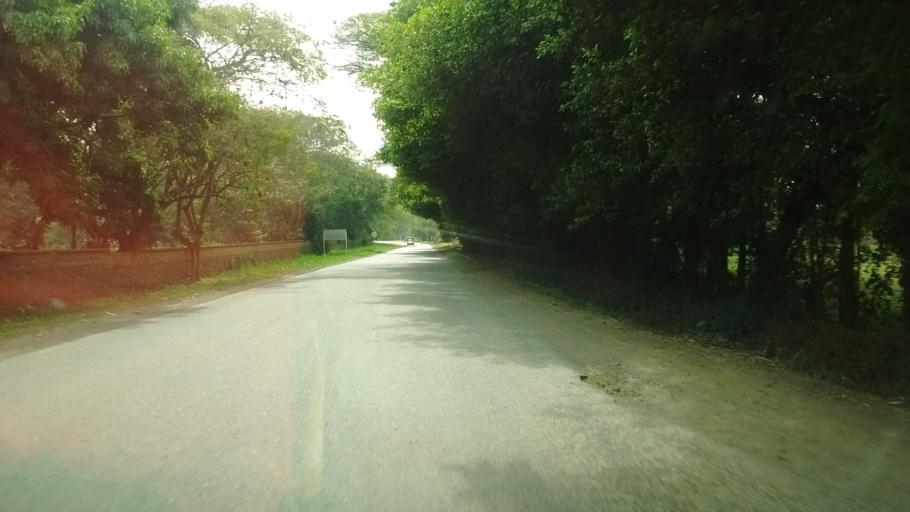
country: CO
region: Cauca
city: Caloto
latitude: 3.0474
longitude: -76.4423
